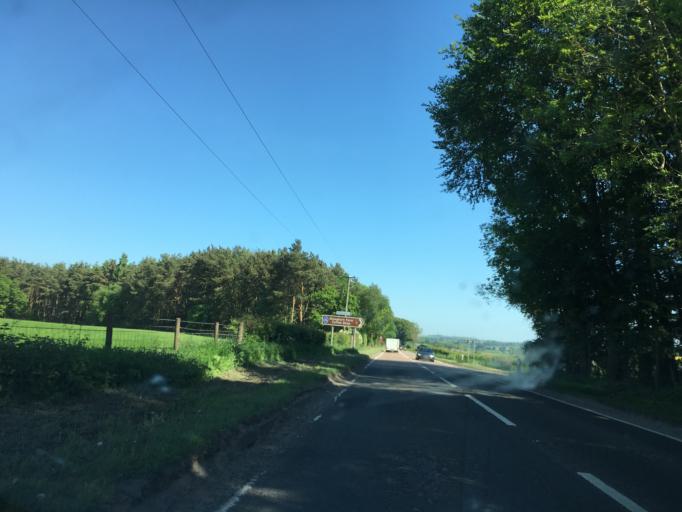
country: GB
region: Scotland
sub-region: Perth and Kinross
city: Methven
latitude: 56.4089
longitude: -3.5426
